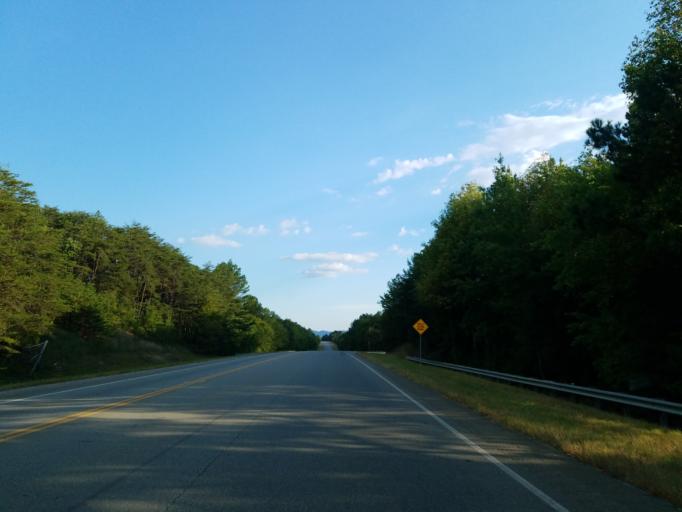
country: US
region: Georgia
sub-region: Murray County
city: Chatsworth
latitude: 34.6830
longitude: -84.7289
